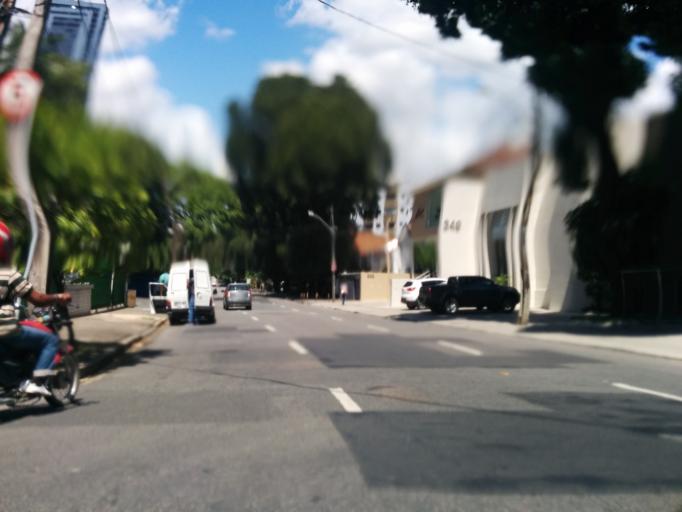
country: BR
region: Pernambuco
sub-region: Recife
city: Recife
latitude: -8.0438
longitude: -34.8987
